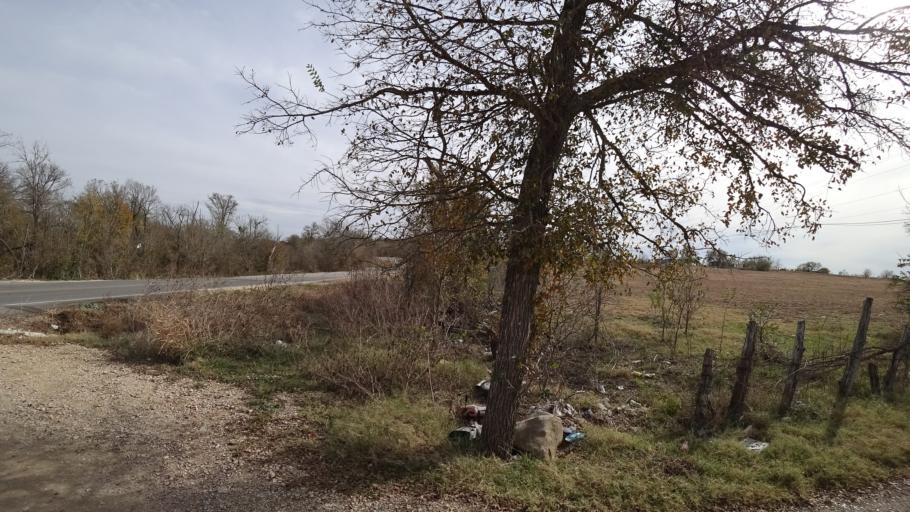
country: US
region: Texas
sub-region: Travis County
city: Garfield
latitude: 30.1305
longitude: -97.6054
